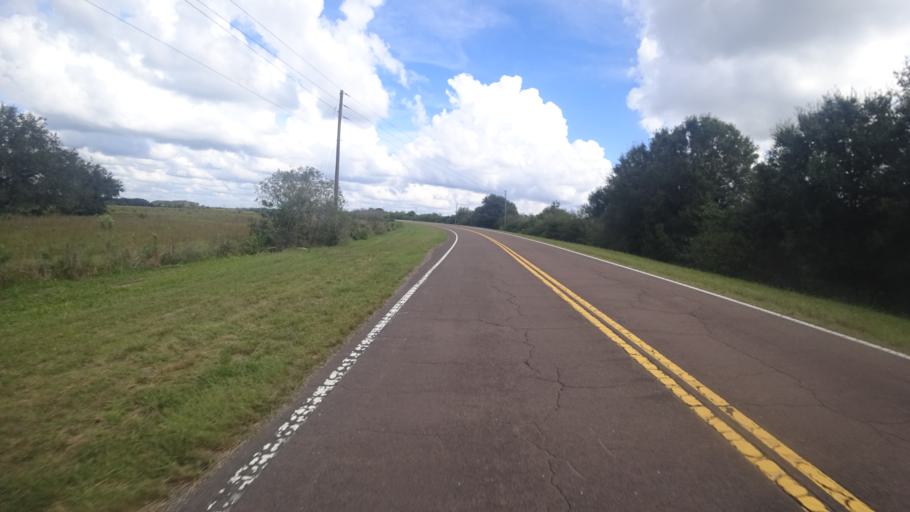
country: US
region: Florida
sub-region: Hillsborough County
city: Ruskin
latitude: 27.6539
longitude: -82.4513
